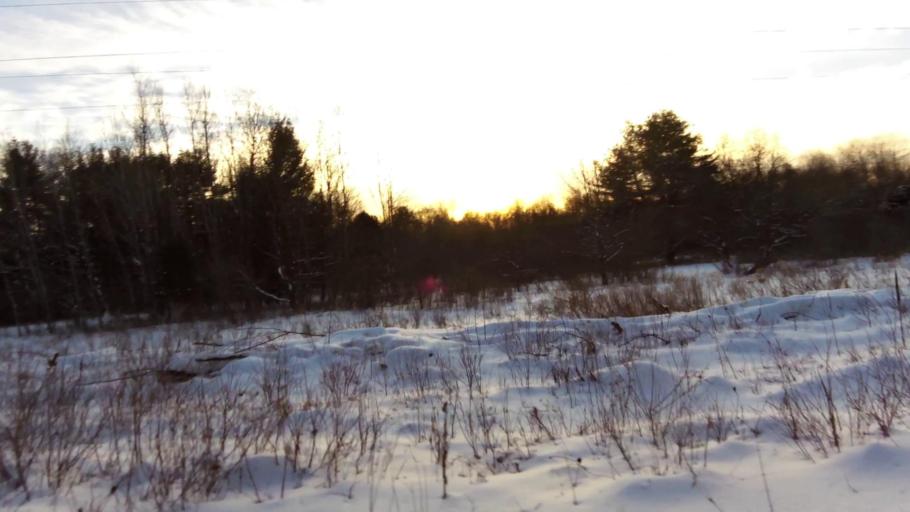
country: US
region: New York
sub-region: Chautauqua County
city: Celoron
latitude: 42.2021
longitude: -79.2585
